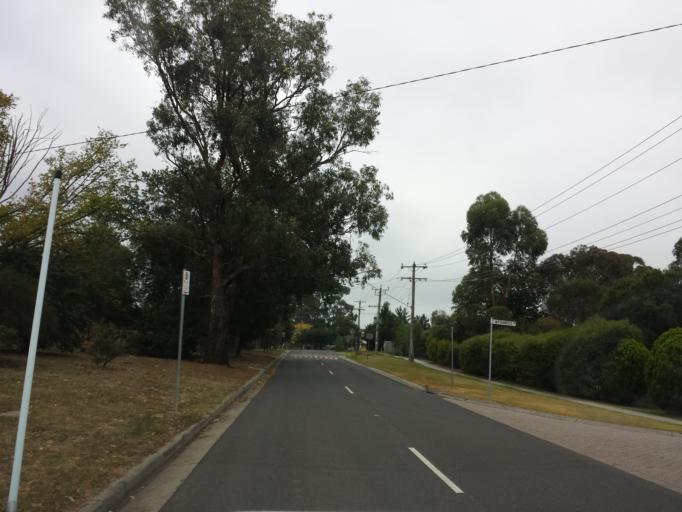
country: AU
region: Victoria
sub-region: Yarra Ranges
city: Yarra Glen
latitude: -37.6529
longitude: 145.3786
